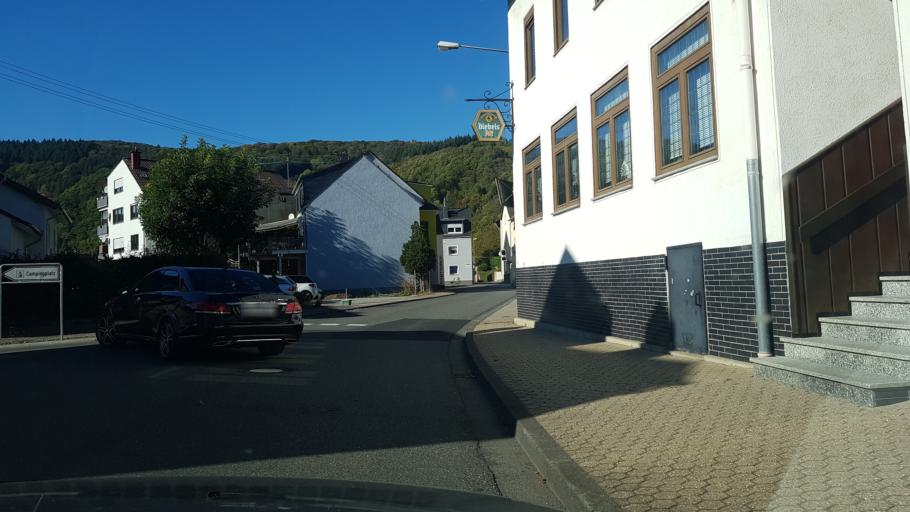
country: DE
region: Rheinland-Pfalz
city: Fachbach
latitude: 50.3376
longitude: 7.6924
